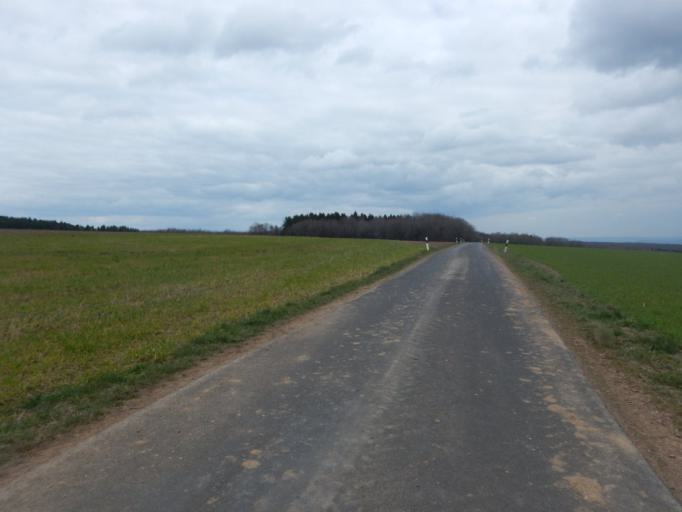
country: LU
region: Diekirch
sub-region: Canton de Redange
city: Rambrouch
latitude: 49.8035
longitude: 5.8401
